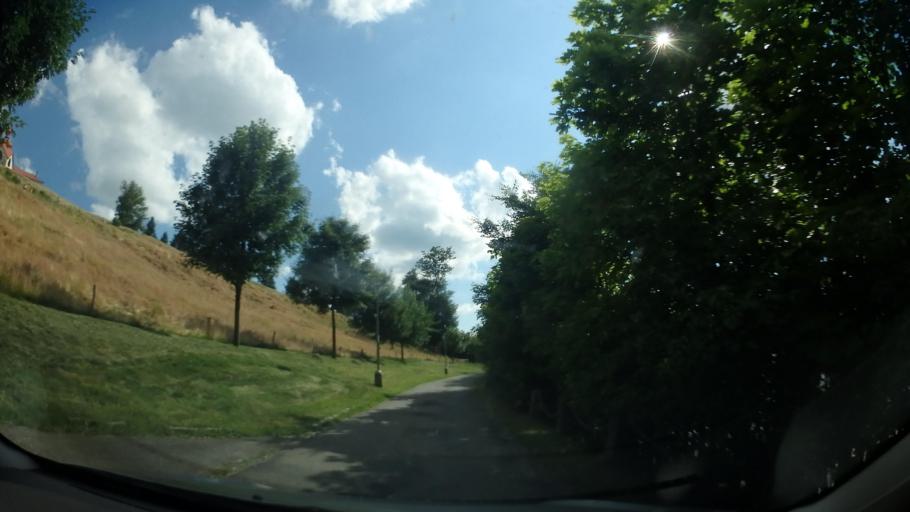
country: CZ
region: Vysocina
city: Zd'ar nad Sazavou Druhy
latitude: 49.5815
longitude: 15.9409
